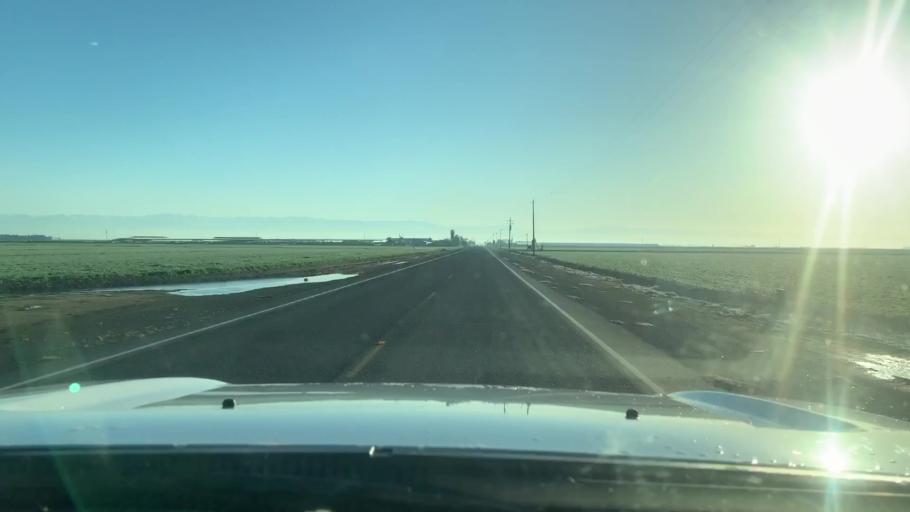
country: US
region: California
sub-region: Kings County
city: Corcoran
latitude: 36.2111
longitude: -119.5543
